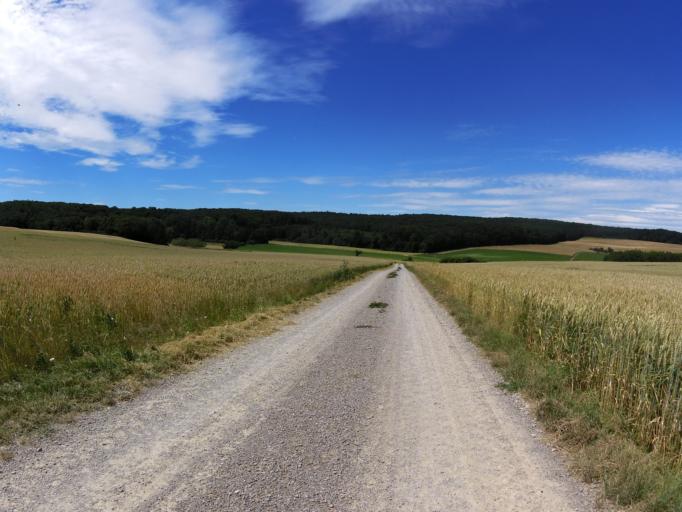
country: DE
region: Bavaria
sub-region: Regierungsbezirk Unterfranken
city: Reichenberg
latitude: 49.7180
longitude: 9.9060
